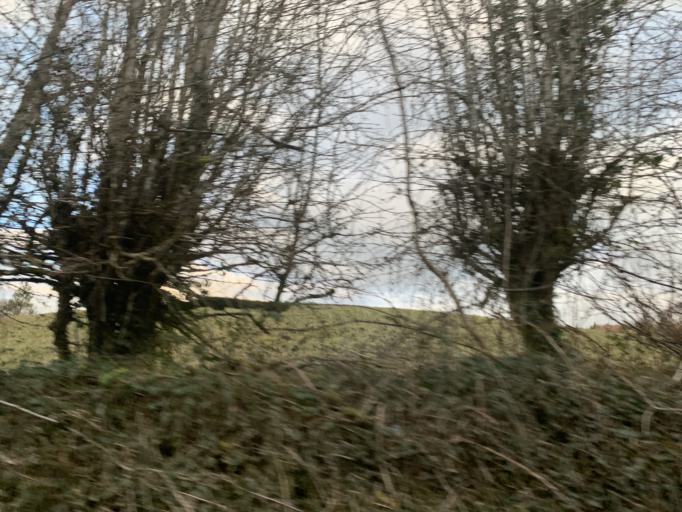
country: IE
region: Connaught
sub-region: Maigh Eo
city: Ballyhaunis
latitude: 53.8369
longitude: -8.7133
